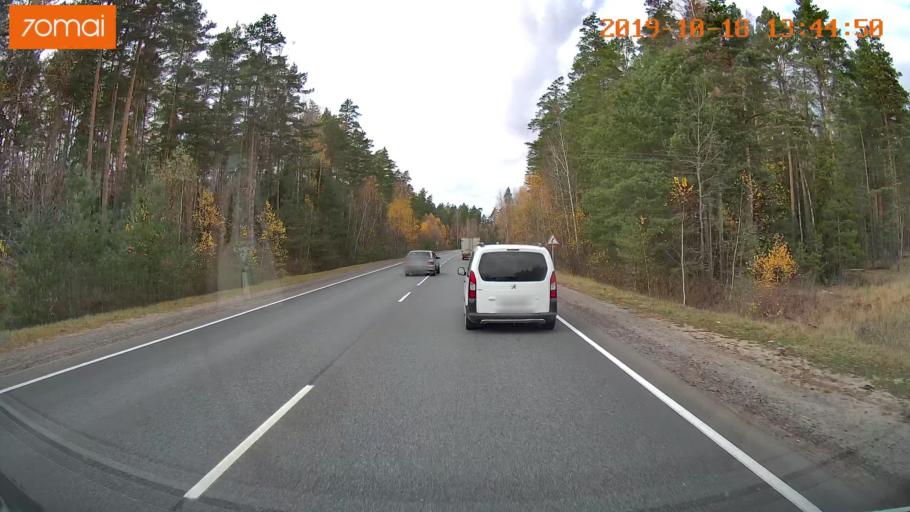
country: RU
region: Rjazan
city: Solotcha
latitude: 54.9399
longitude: 39.9552
